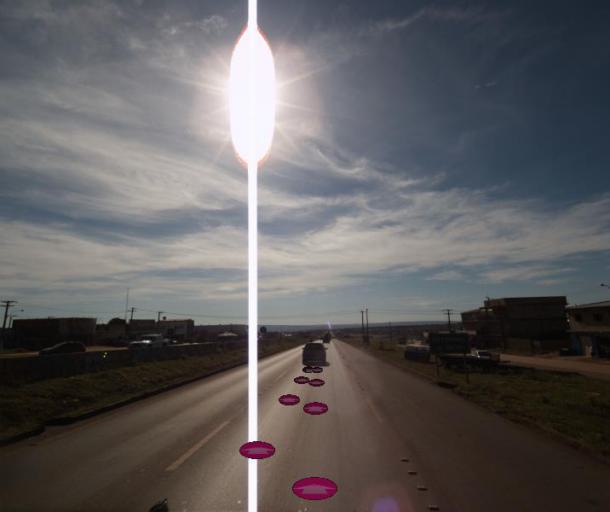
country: BR
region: Federal District
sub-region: Brasilia
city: Brasilia
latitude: -15.7359
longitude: -48.2831
